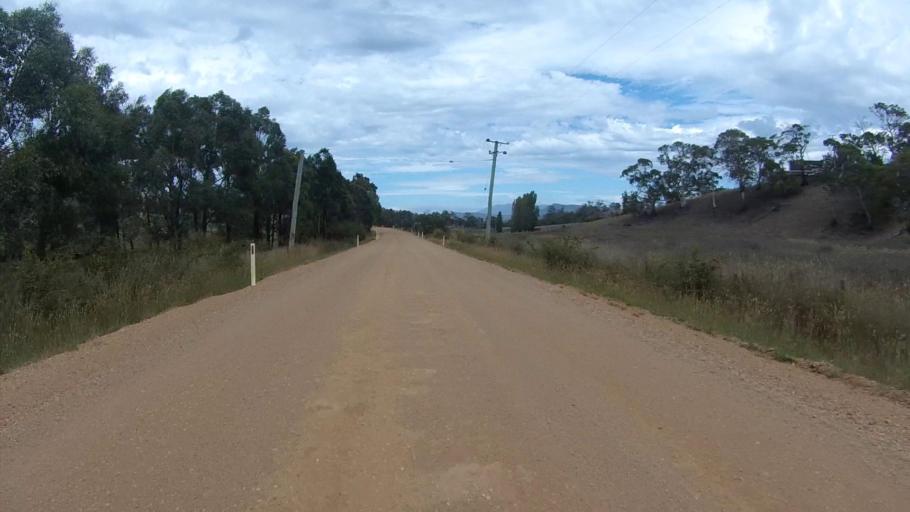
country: AU
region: Tasmania
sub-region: Sorell
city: Sorell
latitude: -42.6940
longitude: 147.4643
